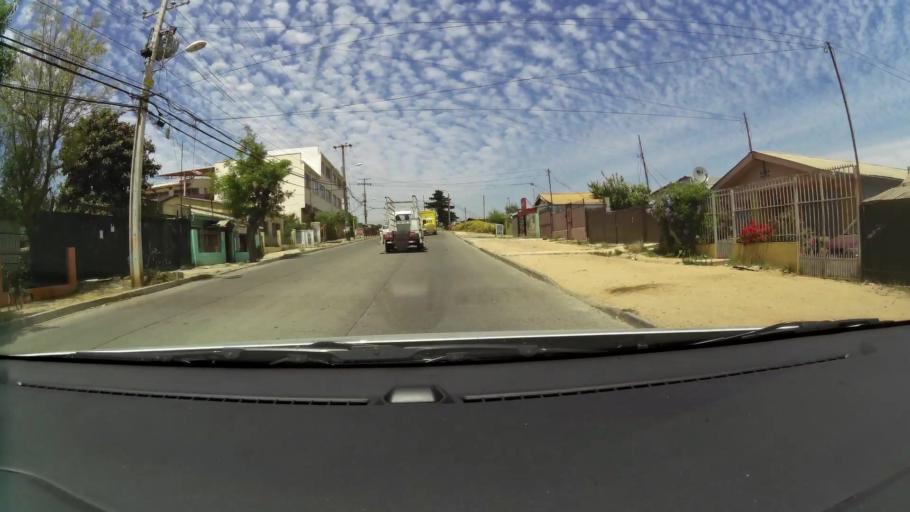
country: CL
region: Valparaiso
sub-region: Provincia de Valparaiso
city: Vina del Mar
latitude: -33.0519
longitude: -71.5718
